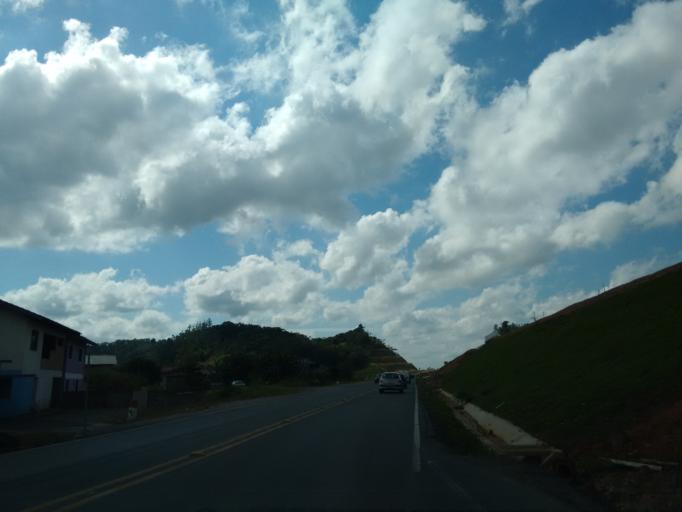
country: BR
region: Santa Catarina
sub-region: Gaspar
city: Gaspar
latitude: -26.9144
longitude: -48.9732
